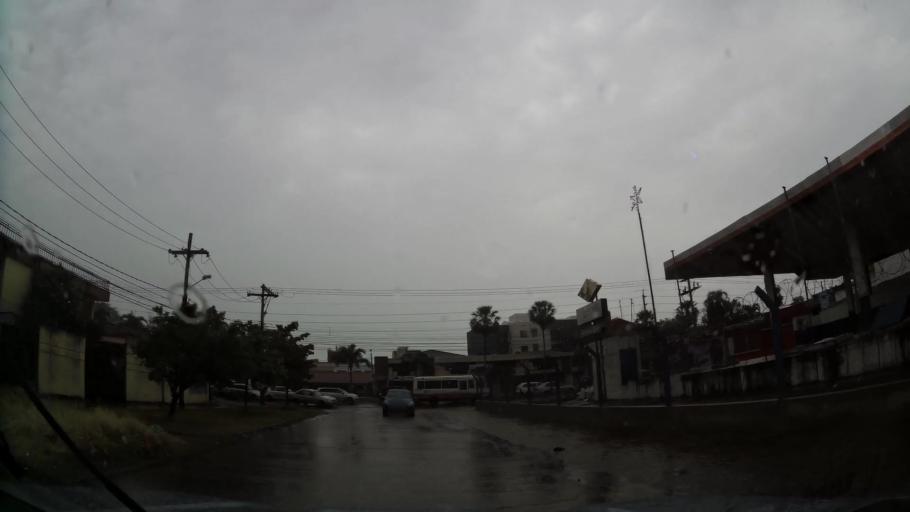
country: BO
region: Santa Cruz
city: Santa Cruz de la Sierra
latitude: -17.7848
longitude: -63.2027
